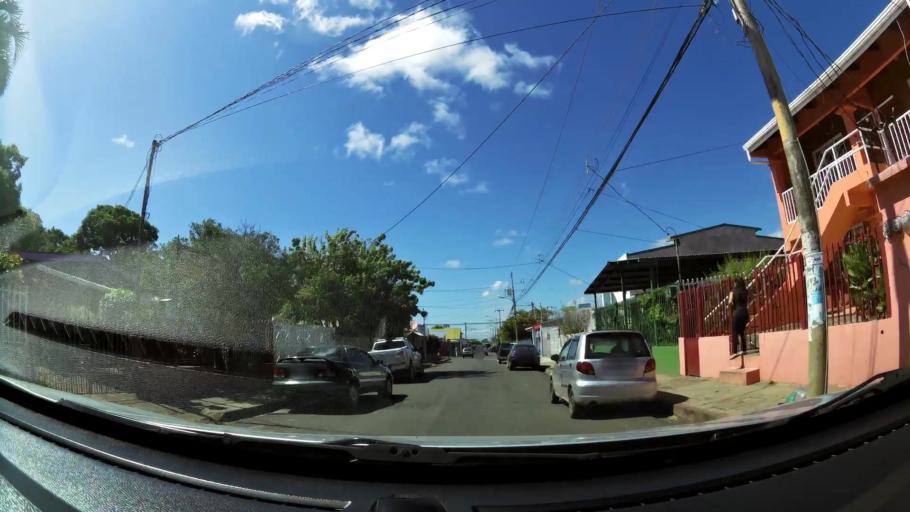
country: CR
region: Guanacaste
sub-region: Canton de Canas
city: Canas
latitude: 10.4280
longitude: -85.0888
